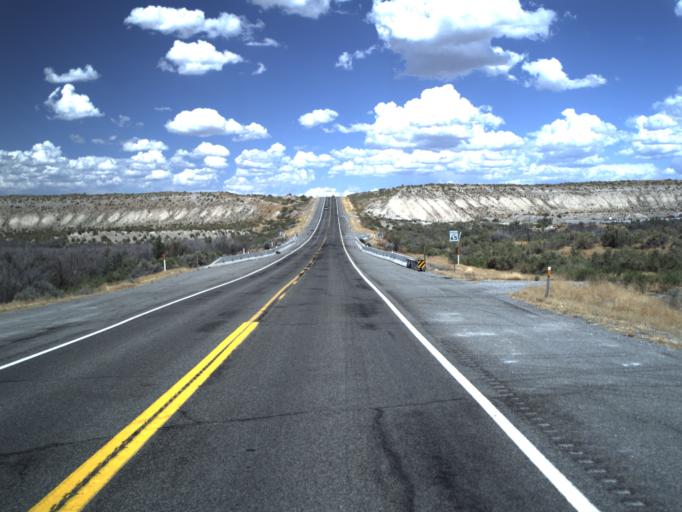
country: US
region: Utah
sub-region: Millard County
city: Delta
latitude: 39.3995
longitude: -112.5002
